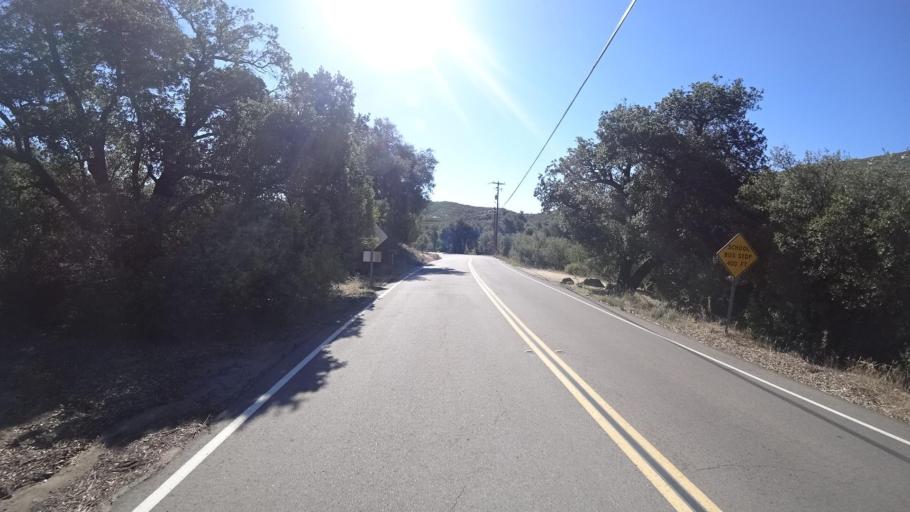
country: US
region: California
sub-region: San Diego County
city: Descanso
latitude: 32.8568
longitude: -116.6303
